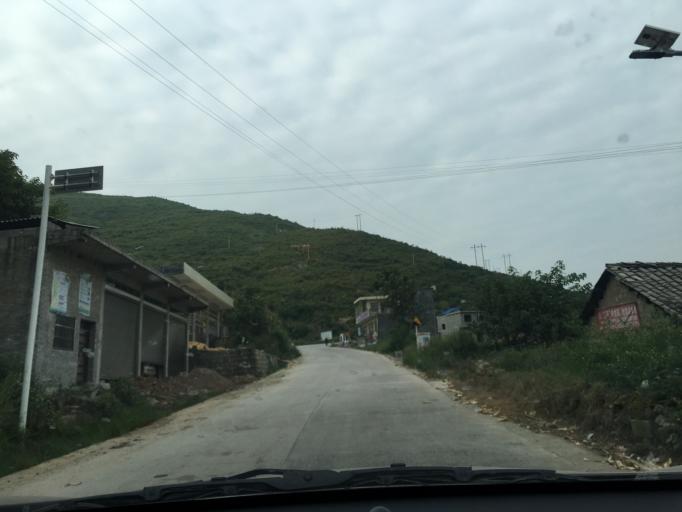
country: CN
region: Guangxi Zhuangzu Zizhiqu
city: Xinzhou
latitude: 25.4361
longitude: 105.4774
